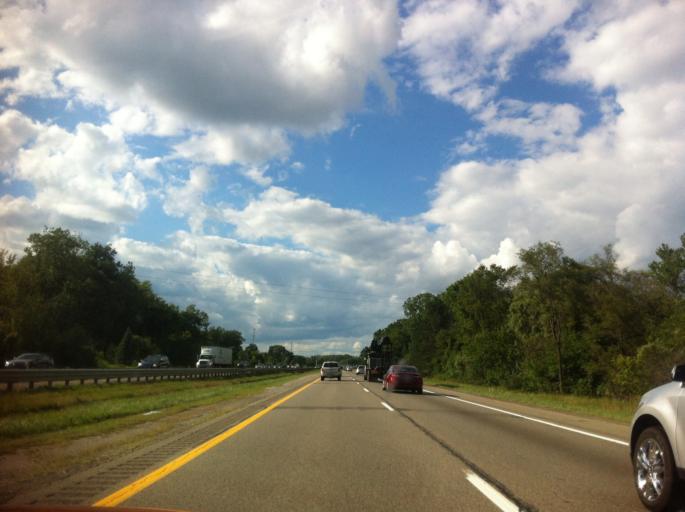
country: US
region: Michigan
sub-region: Livingston County
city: Whitmore Lake
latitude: 42.4141
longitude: -83.7648
